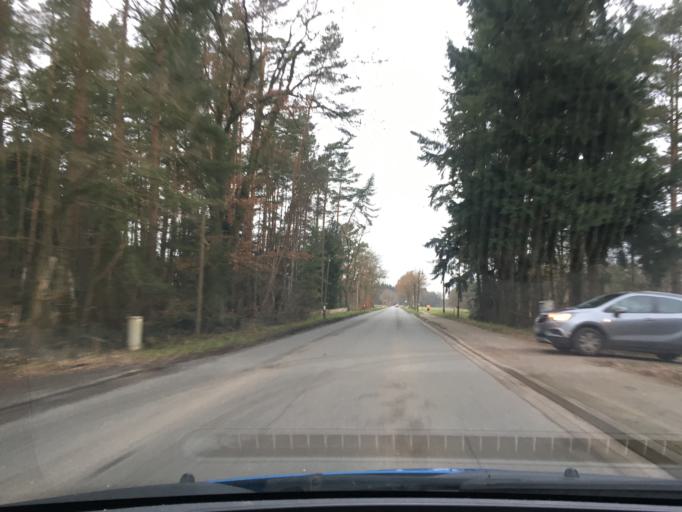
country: DE
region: Lower Saxony
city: Vogelsen
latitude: 53.2945
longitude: 10.3542
